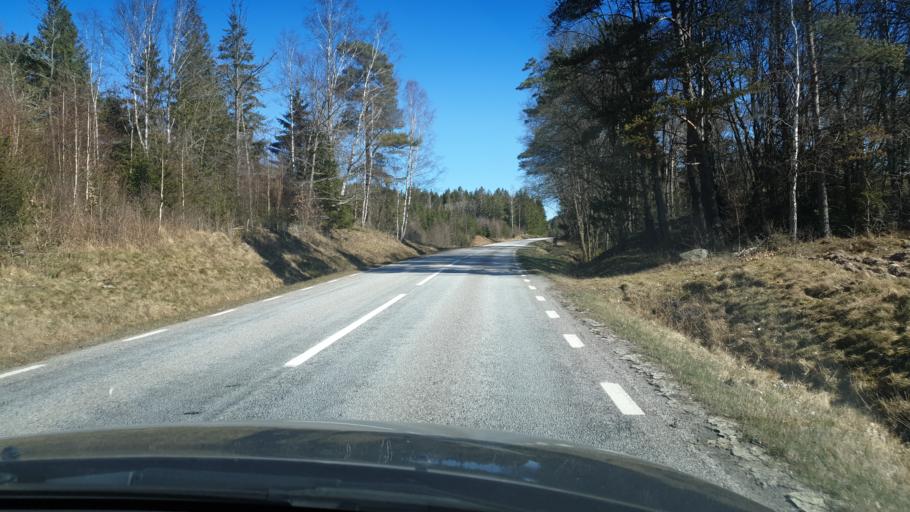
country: SE
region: Vaestra Goetaland
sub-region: Tanums Kommun
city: Tanumshede
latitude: 58.7296
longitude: 11.3949
